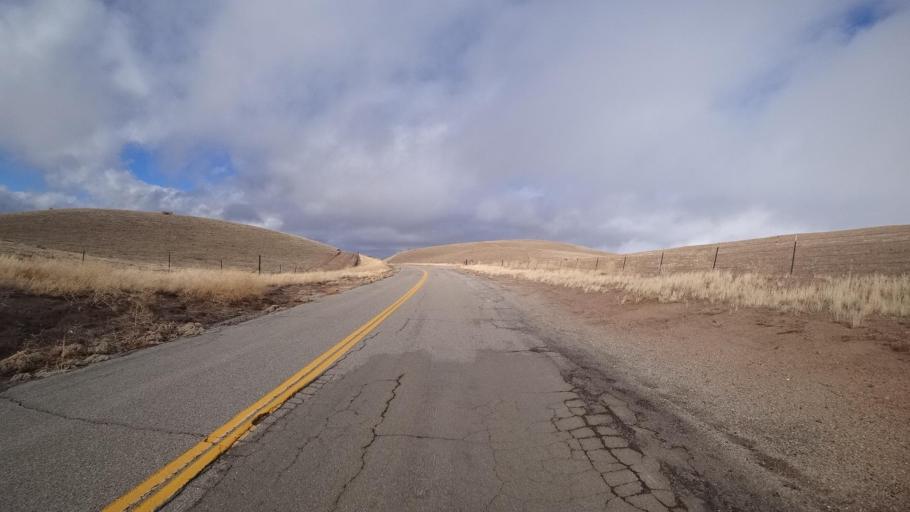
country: US
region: California
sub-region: Kern County
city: Maricopa
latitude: 34.9023
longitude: -119.3701
